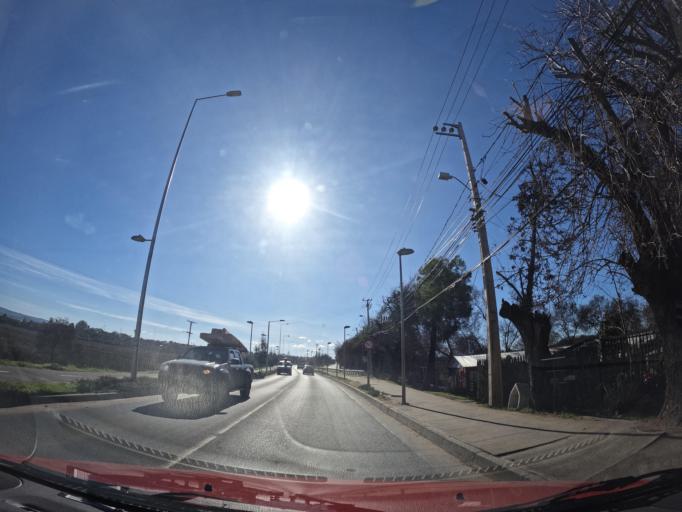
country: CL
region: Maule
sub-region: Provincia de Cauquenes
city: Cauquenes
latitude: -35.9794
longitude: -72.3153
